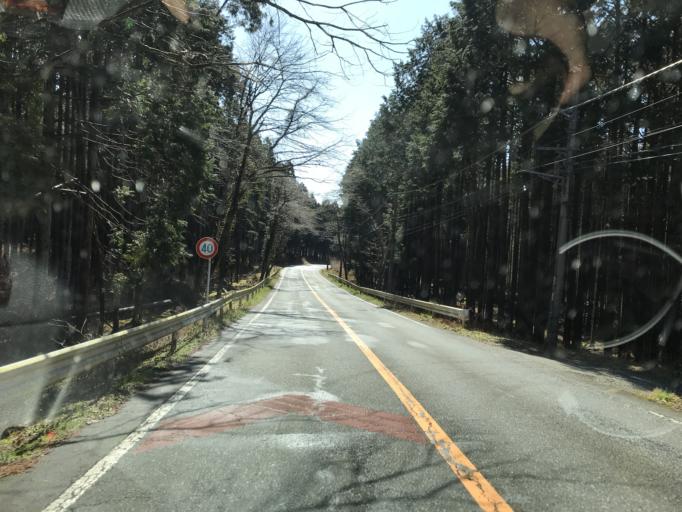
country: JP
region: Shizuoka
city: Fujinomiya
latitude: 35.2900
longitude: 138.6616
